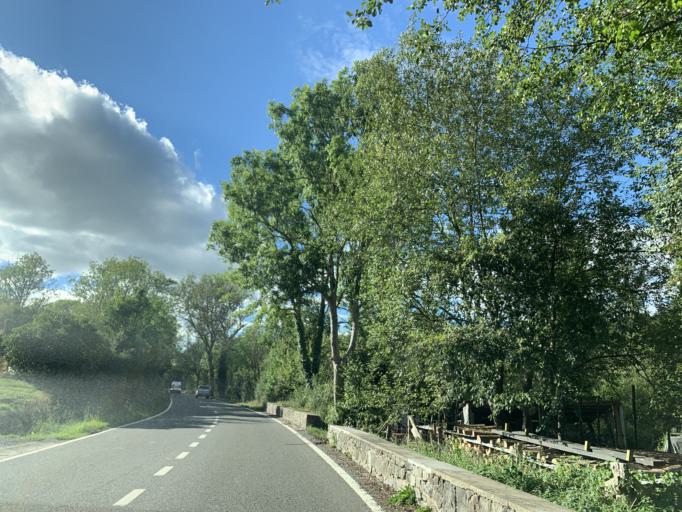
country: BE
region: Wallonia
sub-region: Province du Luxembourg
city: Tellin
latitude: 50.0946
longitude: 5.2750
